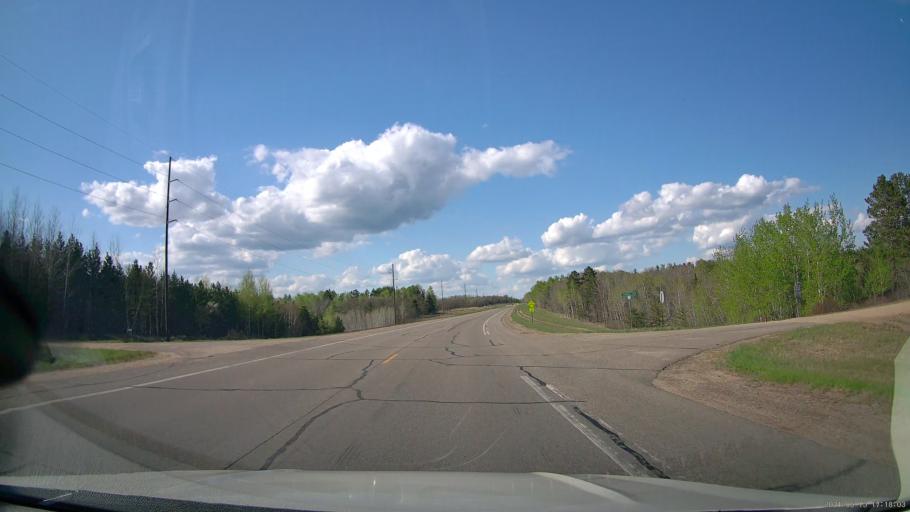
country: US
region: Minnesota
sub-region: Hubbard County
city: Park Rapids
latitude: 46.9550
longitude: -95.0183
